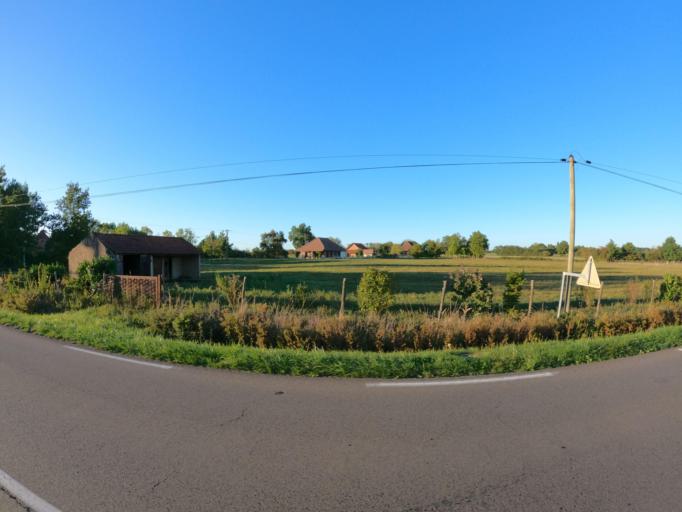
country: FR
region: Bourgogne
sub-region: Departement de Saone-et-Loire
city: Saint-Martin-en-Bresse
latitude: 46.7433
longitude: 5.1105
